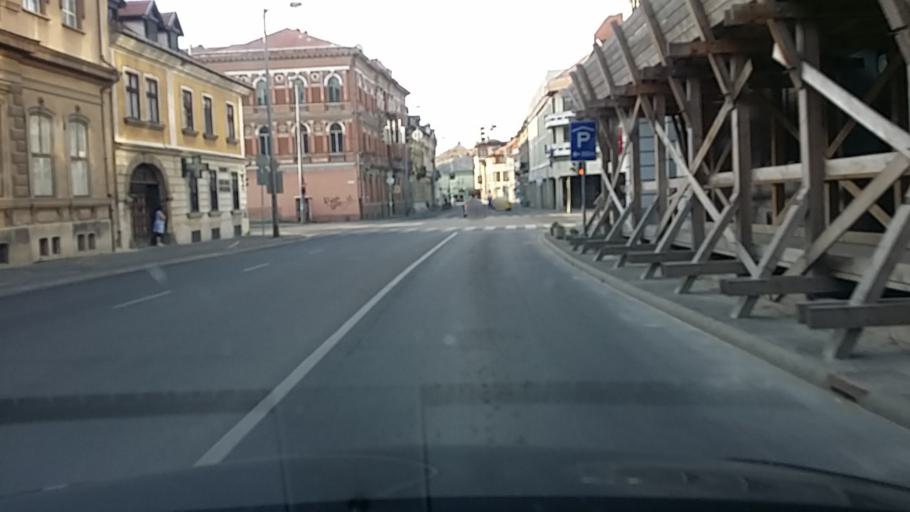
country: HU
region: Borsod-Abauj-Zemplen
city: Miskolc
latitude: 48.1004
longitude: 20.7852
